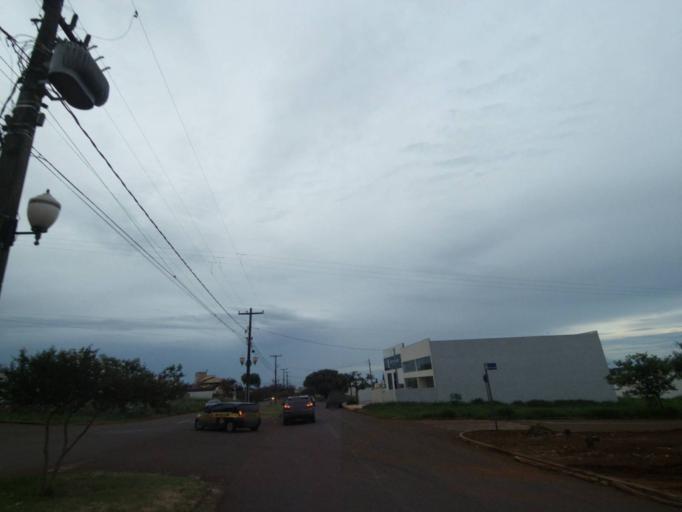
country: BR
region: Parana
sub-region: Campo Mourao
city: Campo Mourao
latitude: -24.0363
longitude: -52.3625
